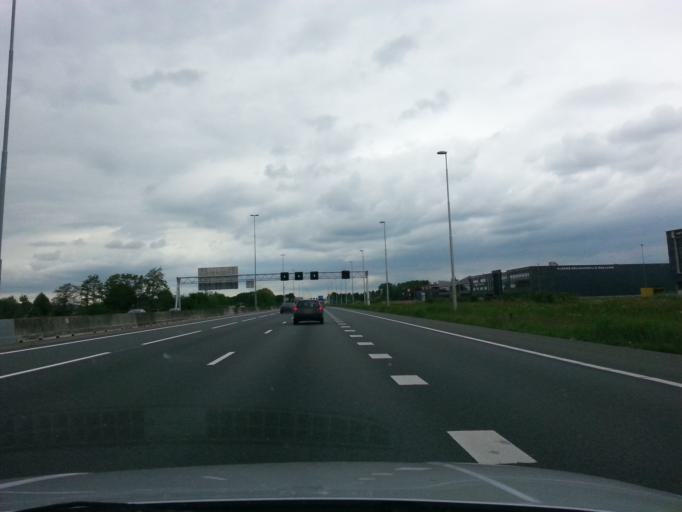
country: NL
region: Gelderland
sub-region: Gemeente Ede
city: Ederveen
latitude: 52.0284
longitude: 5.6053
